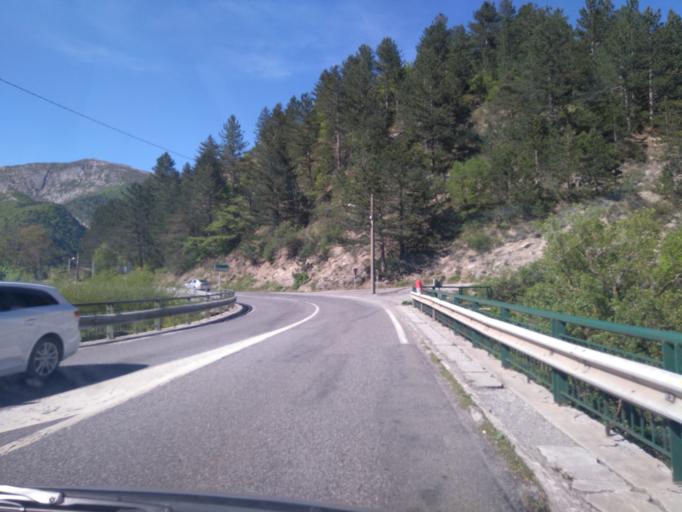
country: FR
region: Provence-Alpes-Cote d'Azur
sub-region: Departement des Hautes-Alpes
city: Serres
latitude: 44.4321
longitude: 5.7132
